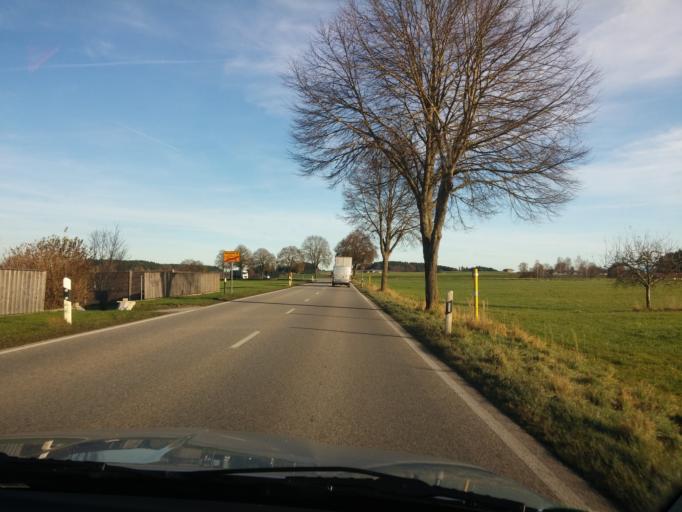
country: DE
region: Bavaria
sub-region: Upper Bavaria
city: Obing
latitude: 48.0002
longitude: 12.4137
